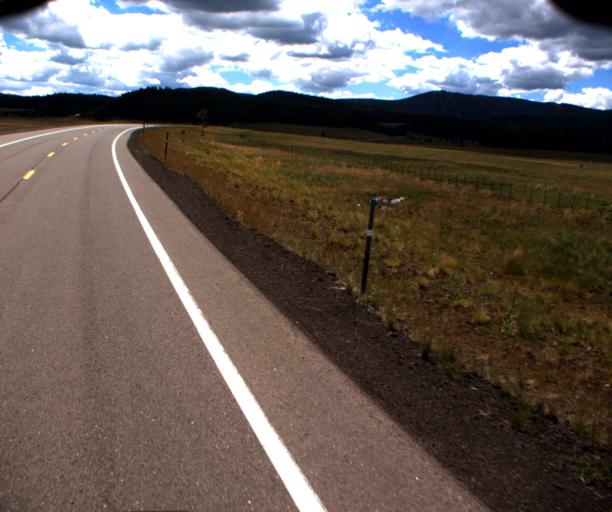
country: US
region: Arizona
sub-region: Apache County
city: Eagar
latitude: 34.0164
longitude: -109.5691
